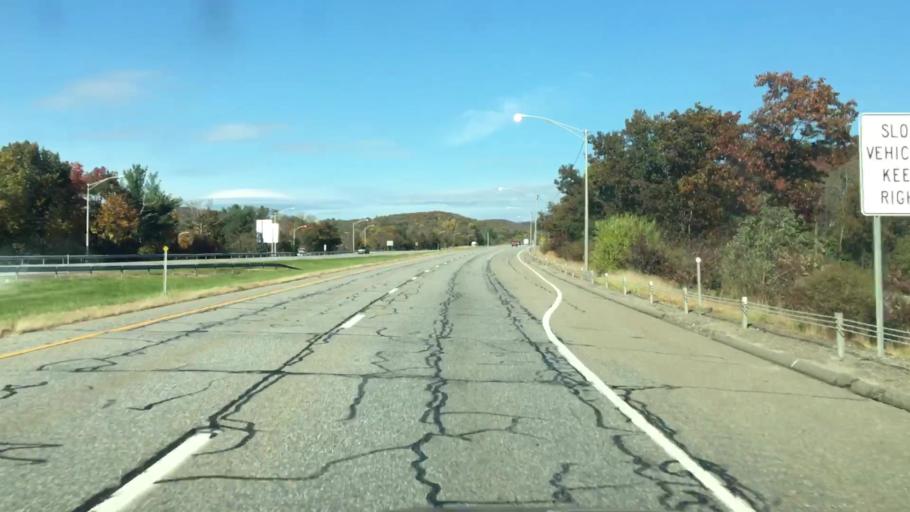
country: US
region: Connecticut
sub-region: Litchfield County
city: Torrington
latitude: 41.8077
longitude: -73.1134
